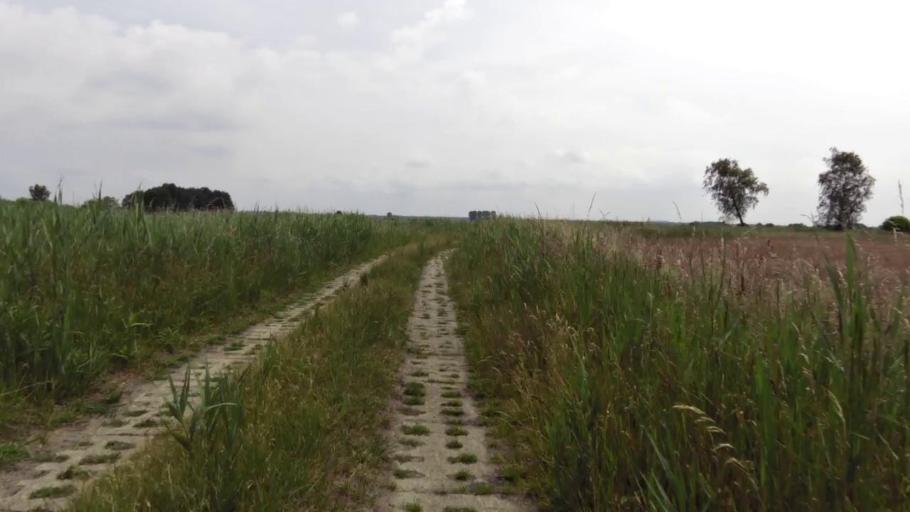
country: PL
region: West Pomeranian Voivodeship
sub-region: Powiat goleniowski
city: Stepnica
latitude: 53.7292
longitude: 14.6035
